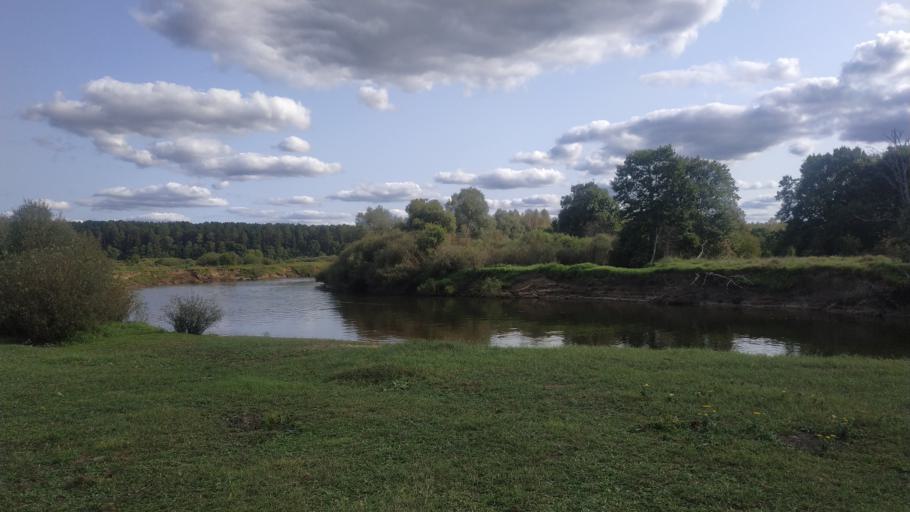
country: RU
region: Brjansk
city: Zhukovka
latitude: 53.5276
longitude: 33.6794
